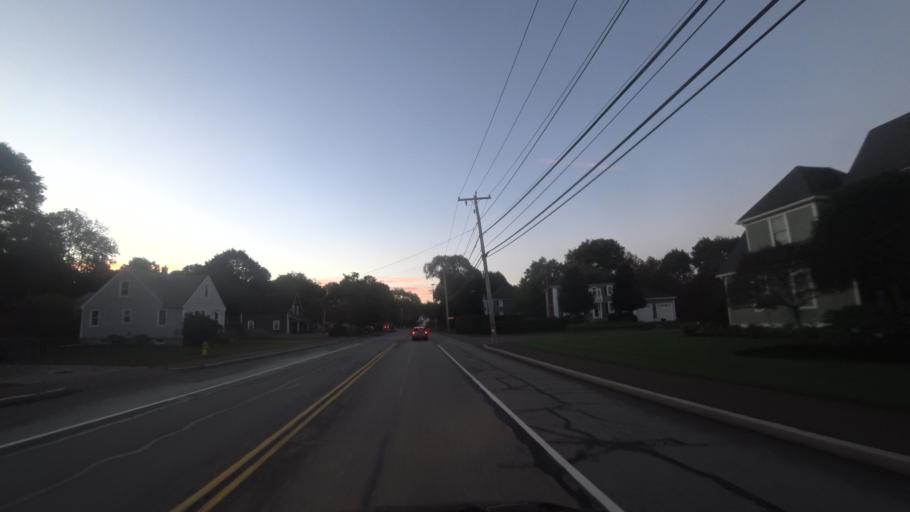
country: US
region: Massachusetts
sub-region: Essex County
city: Saugus
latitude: 42.4759
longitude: -71.0391
